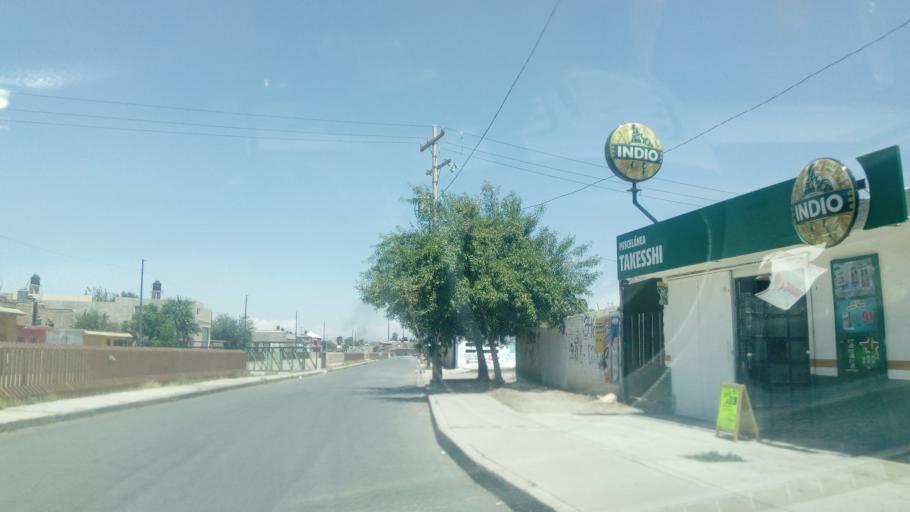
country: MX
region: Durango
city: Victoria de Durango
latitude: 24.0182
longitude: -104.6360
